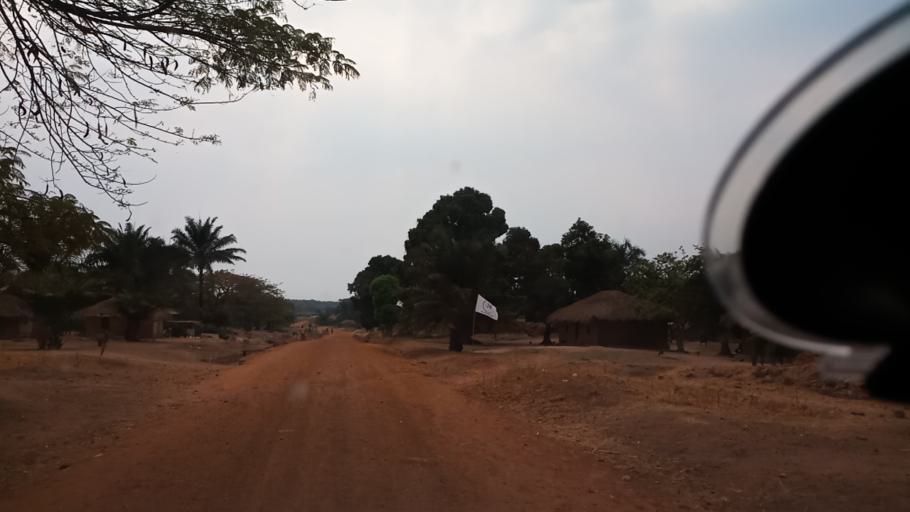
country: ZM
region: Luapula
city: Nchelenge
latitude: -9.0998
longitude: 28.3019
